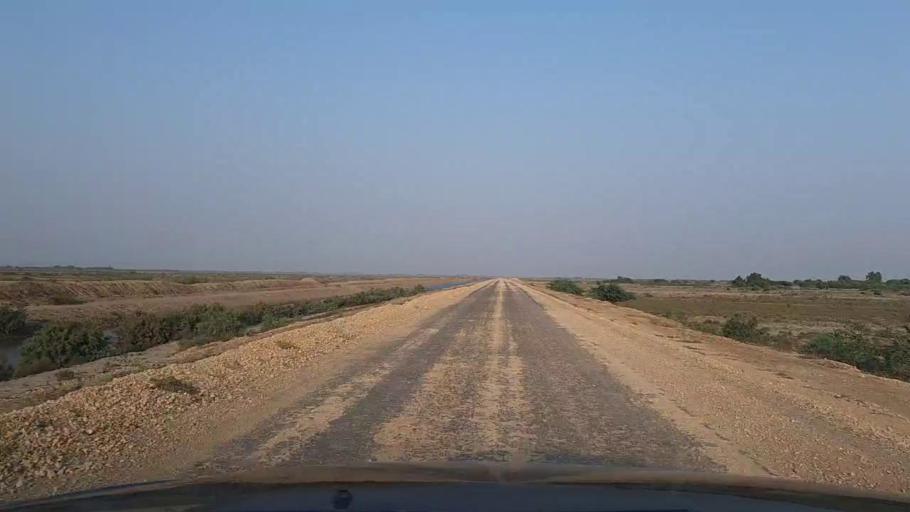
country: PK
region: Sindh
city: Mirpur Sakro
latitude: 24.4246
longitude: 67.7491
